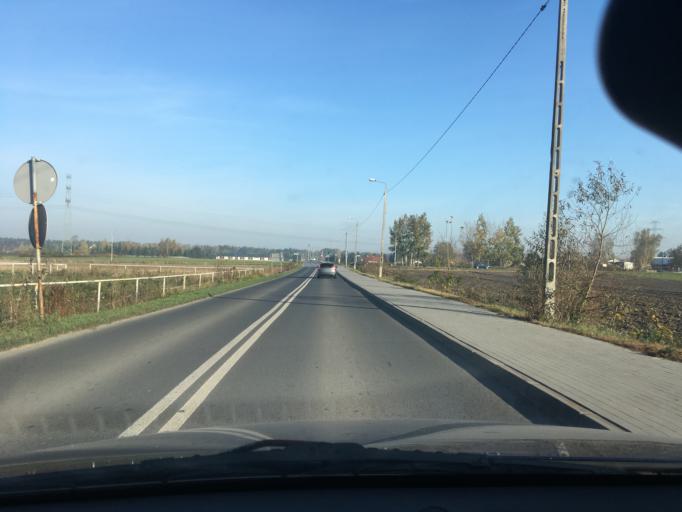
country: PL
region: Masovian Voivodeship
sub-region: Powiat piaseczynski
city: Lesznowola
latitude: 52.0688
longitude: 20.9344
